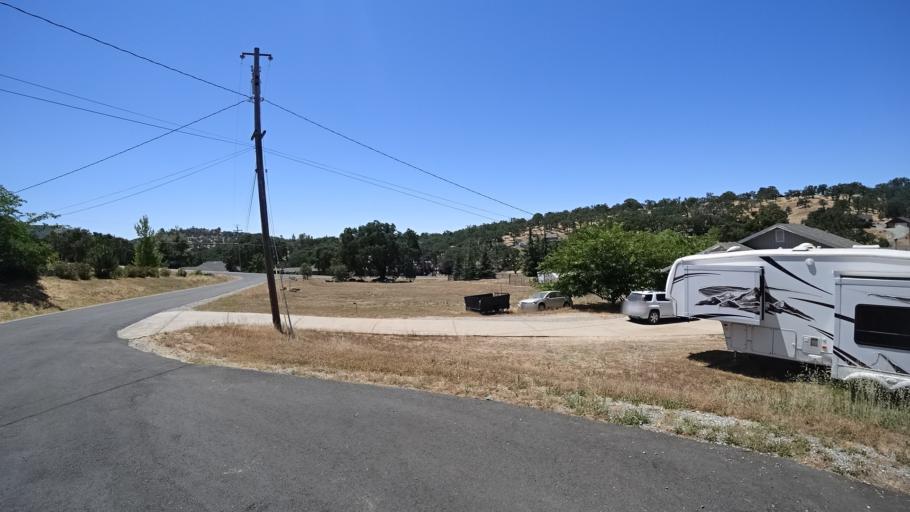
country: US
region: California
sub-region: Calaveras County
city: Rancho Calaveras
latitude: 38.1360
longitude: -120.8463
